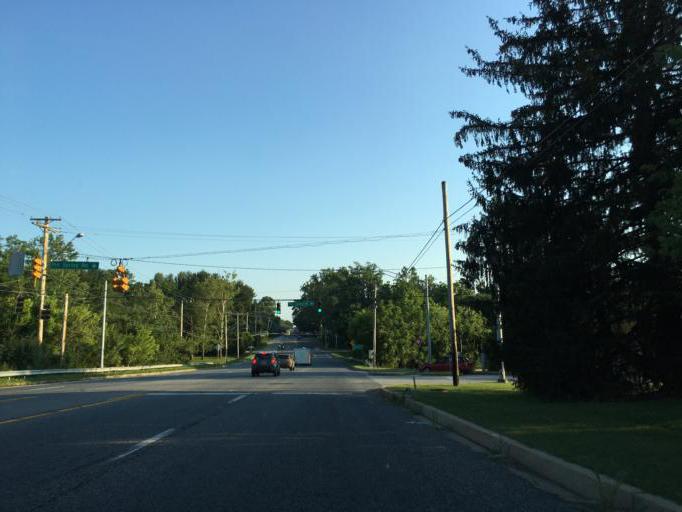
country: US
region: Maryland
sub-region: Baltimore County
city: Hampton
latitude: 39.4263
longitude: -76.5964
